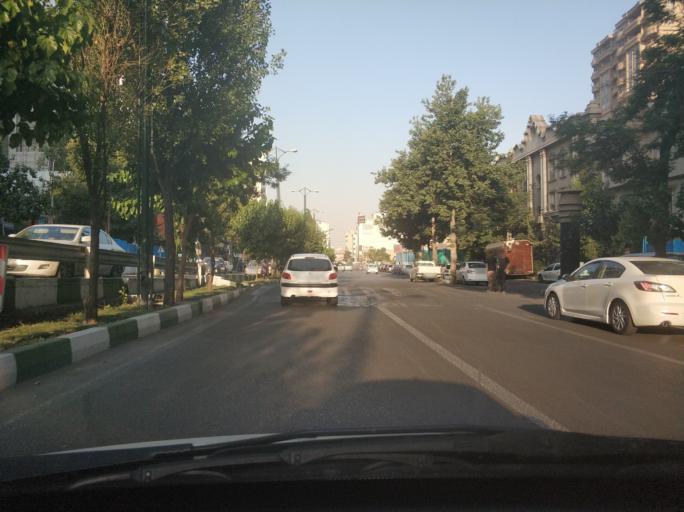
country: IR
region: Tehran
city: Tajrish
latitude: 35.7997
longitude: 51.4697
